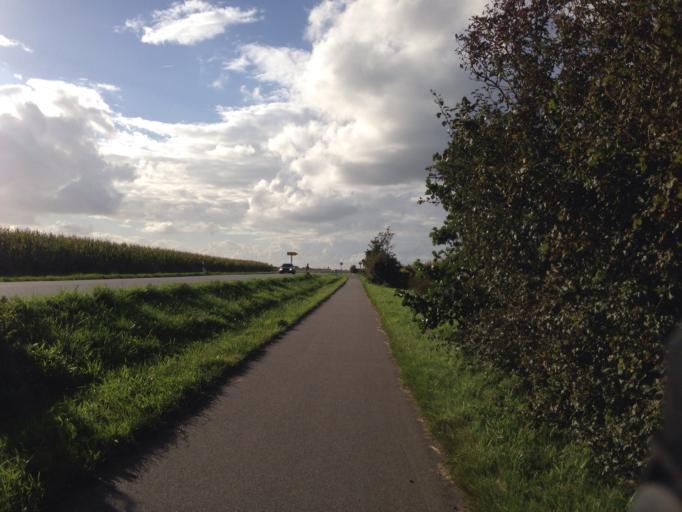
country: DE
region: Schleswig-Holstein
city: Oldsum
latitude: 54.7249
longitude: 8.4673
